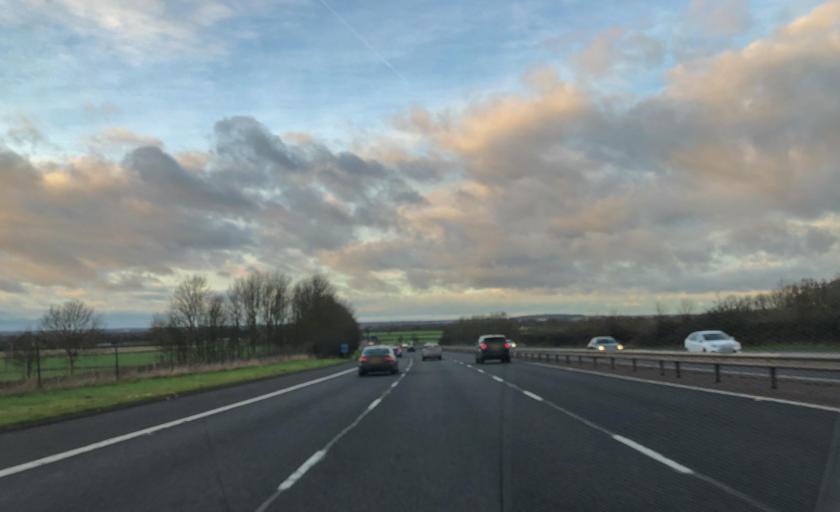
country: GB
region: England
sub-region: Oxfordshire
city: Wheatley
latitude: 51.8247
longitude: -1.1095
